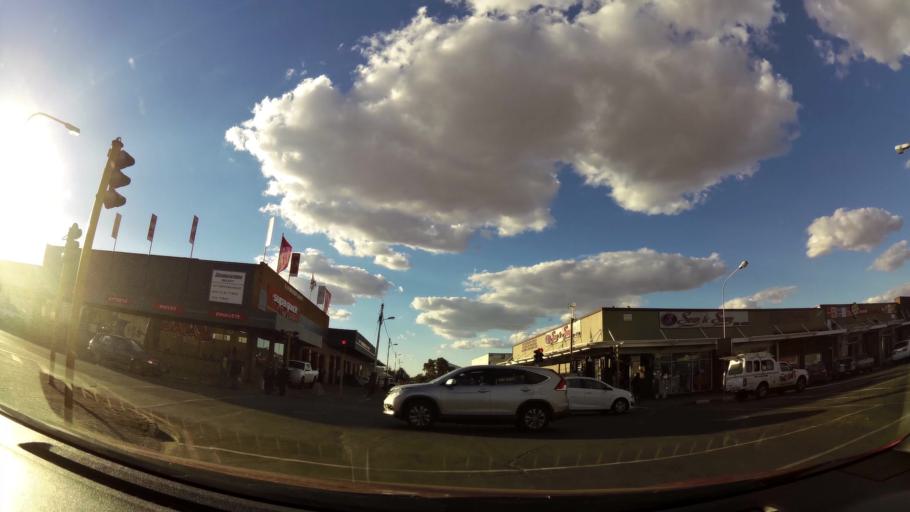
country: ZA
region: North-West
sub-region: Dr Kenneth Kaunda District Municipality
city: Potchefstroom
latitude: -26.7113
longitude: 27.1013
